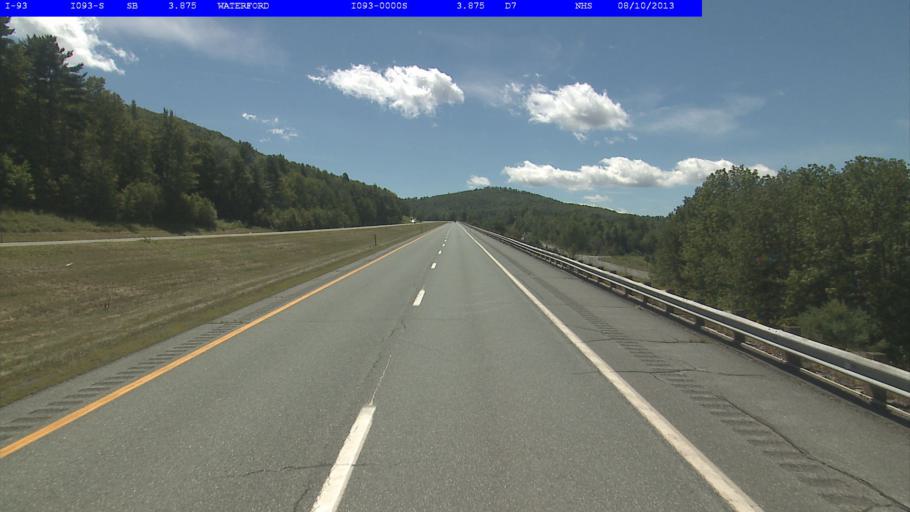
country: US
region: Vermont
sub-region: Caledonia County
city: Saint Johnsbury
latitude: 44.3916
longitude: -71.9217
